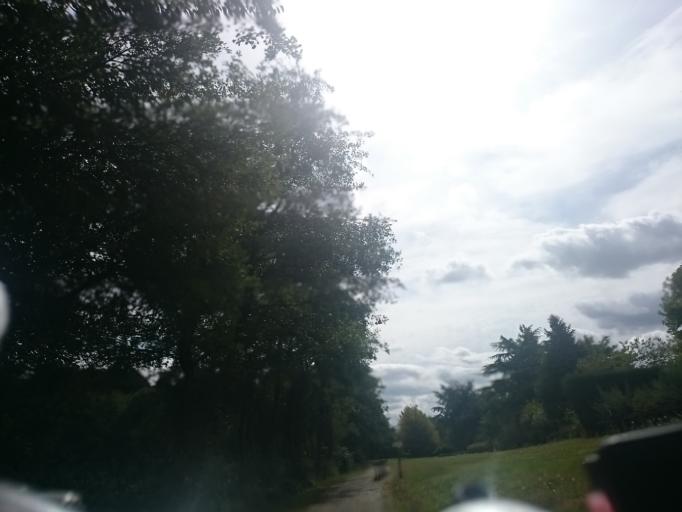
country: FR
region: Brittany
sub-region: Departement d'Ille-et-Vilaine
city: Cesson-Sevigne
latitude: 48.1214
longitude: -1.5915
